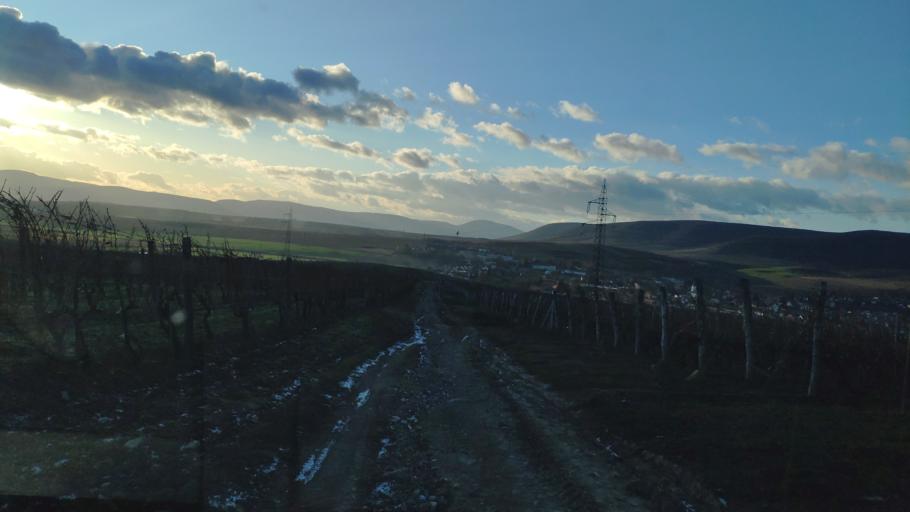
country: HU
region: Borsod-Abauj-Zemplen
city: Tolcsva
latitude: 48.2808
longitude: 21.4701
